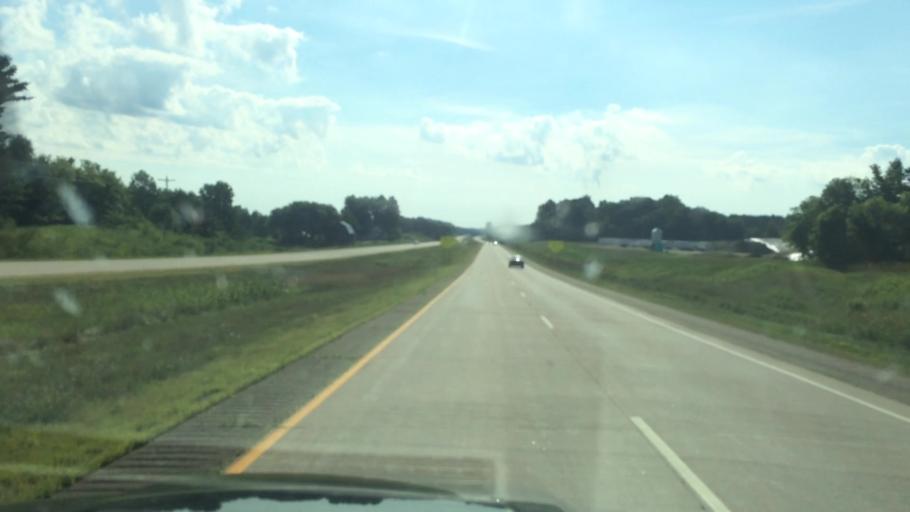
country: US
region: Wisconsin
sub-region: Shawano County
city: Wittenberg
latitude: 44.8259
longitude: -89.0994
